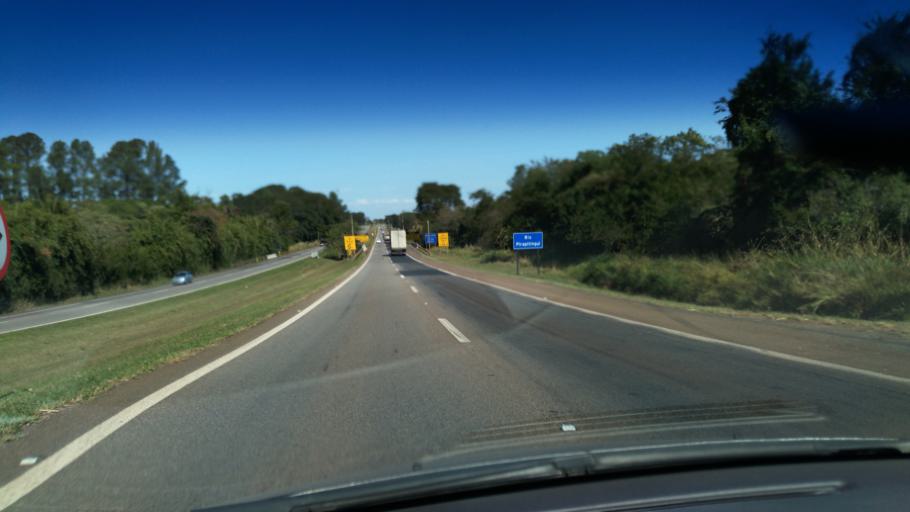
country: BR
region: Sao Paulo
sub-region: Santo Antonio De Posse
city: Santo Antonio de Posse
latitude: -22.5571
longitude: -46.9994
